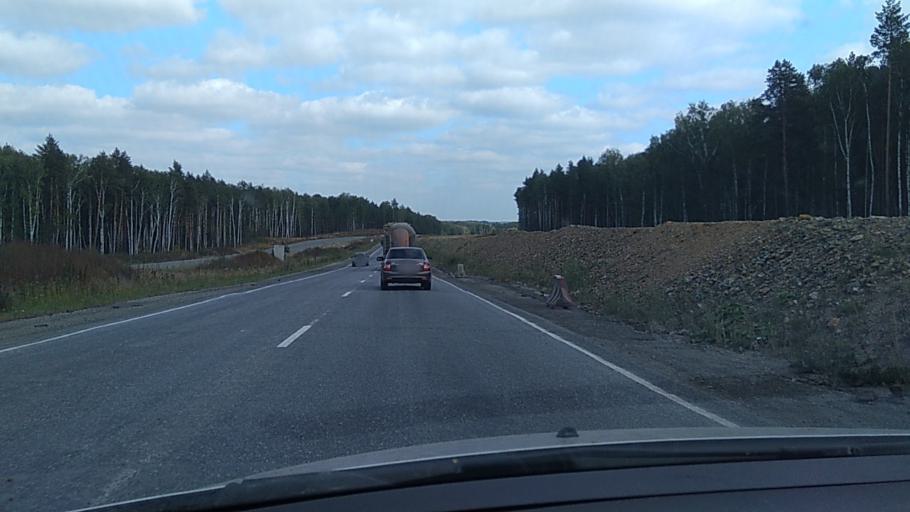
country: RU
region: Chelyabinsk
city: Chebarkul'
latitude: 54.9232
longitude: 60.2767
